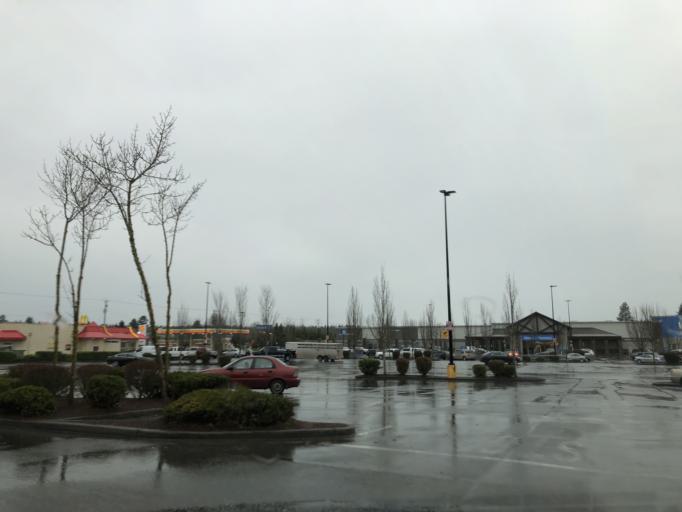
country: US
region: Washington
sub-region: Pierce County
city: Elk Plain
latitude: 47.0724
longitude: -122.4175
